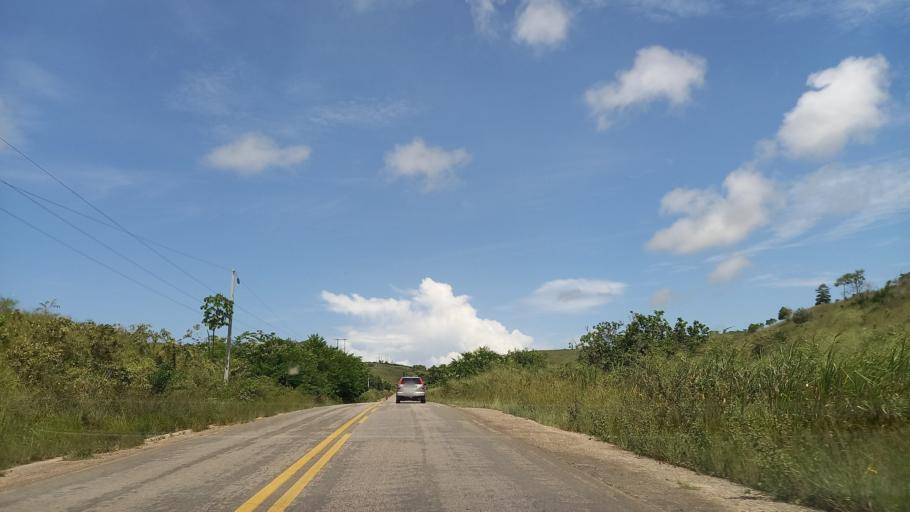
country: BR
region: Pernambuco
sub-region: Barreiros
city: Barreiros
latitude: -8.8367
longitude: -35.1739
